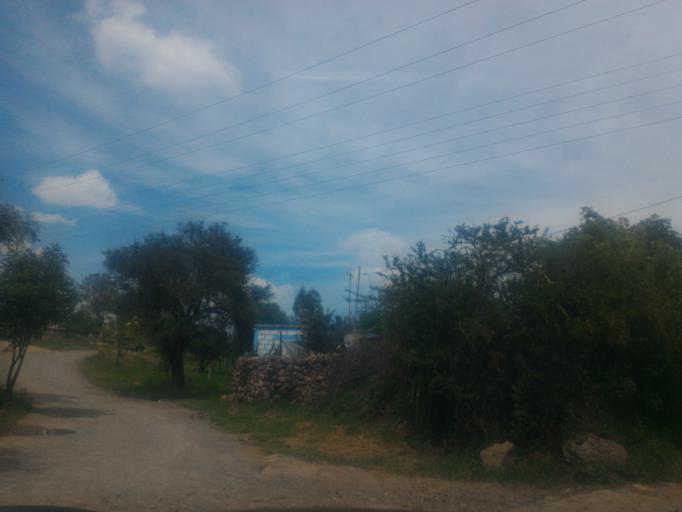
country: MX
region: Guanajuato
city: Ciudad Manuel Doblado
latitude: 20.8043
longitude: -102.0742
